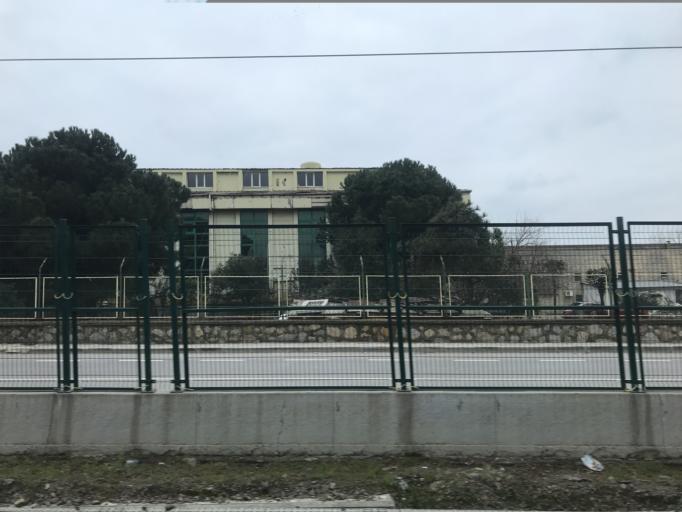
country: TR
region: Kocaeli
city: Darica
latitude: 40.7965
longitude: 29.3840
